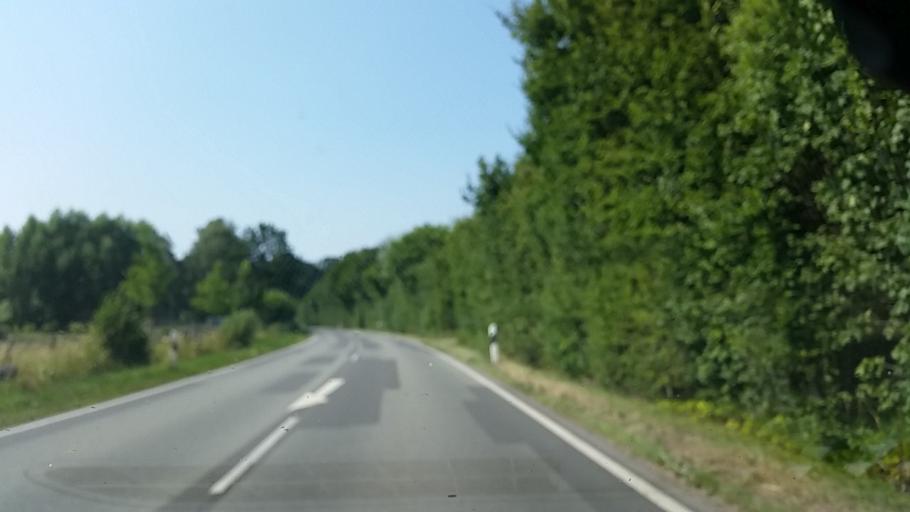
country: DE
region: Schleswig-Holstein
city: Dahmker
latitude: 53.6023
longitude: 10.4456
